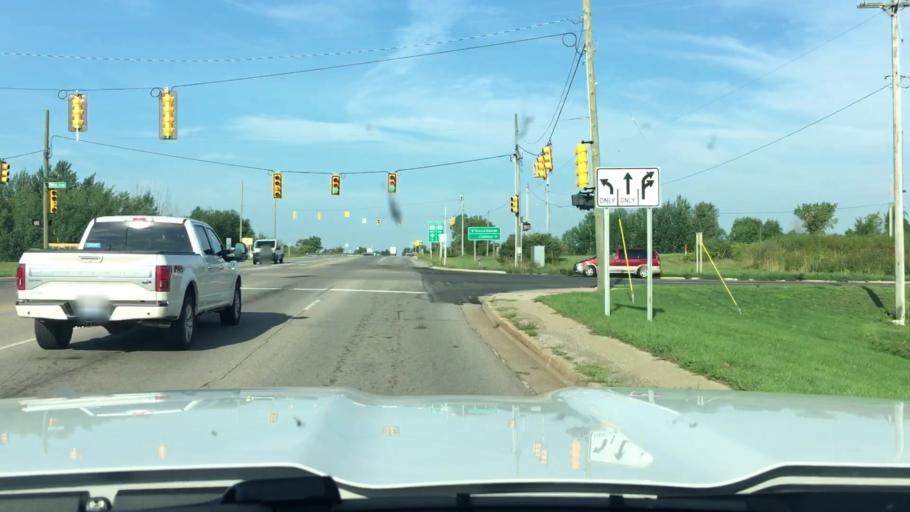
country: US
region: Michigan
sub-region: Kent County
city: Cedar Springs
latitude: 43.2199
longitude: -85.5707
